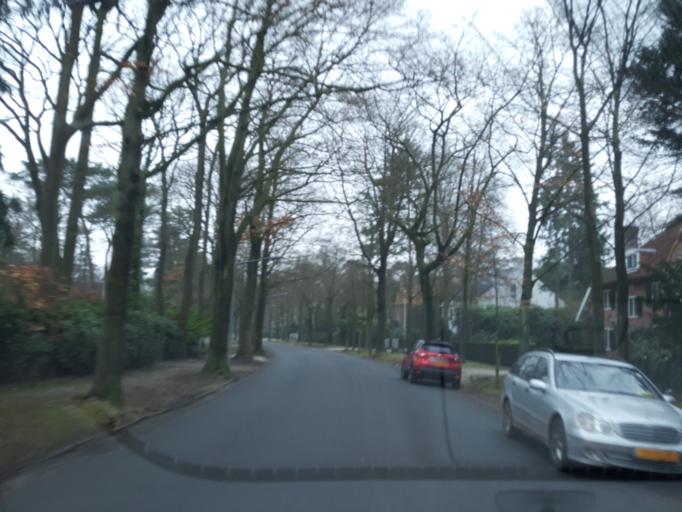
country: NL
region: North Holland
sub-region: Gemeente Hilversum
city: Hilversum
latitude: 52.2383
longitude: 5.1568
